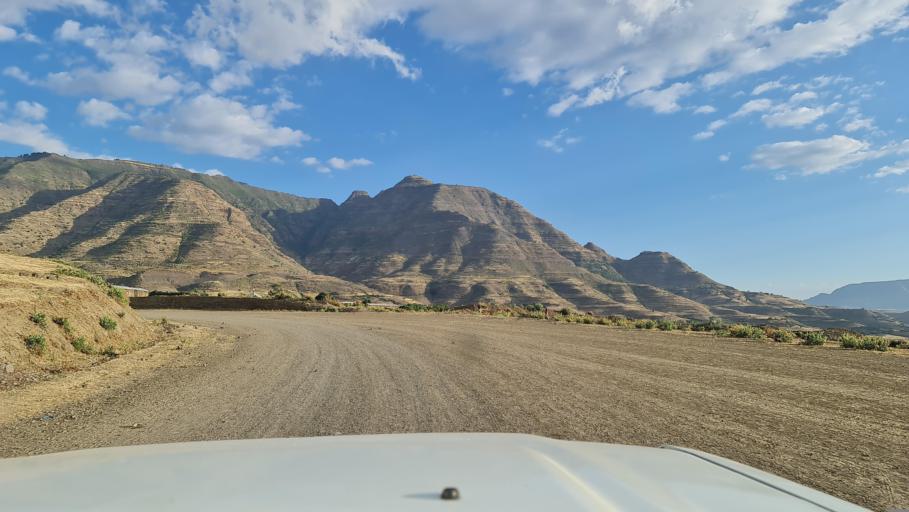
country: ET
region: Amhara
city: Debark'
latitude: 13.0384
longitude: 38.0385
